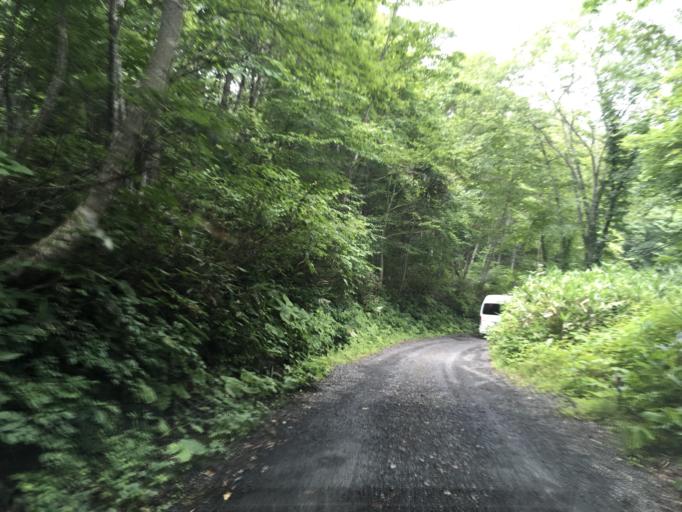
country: JP
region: Iwate
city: Ichinoseki
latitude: 38.9524
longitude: 140.8498
